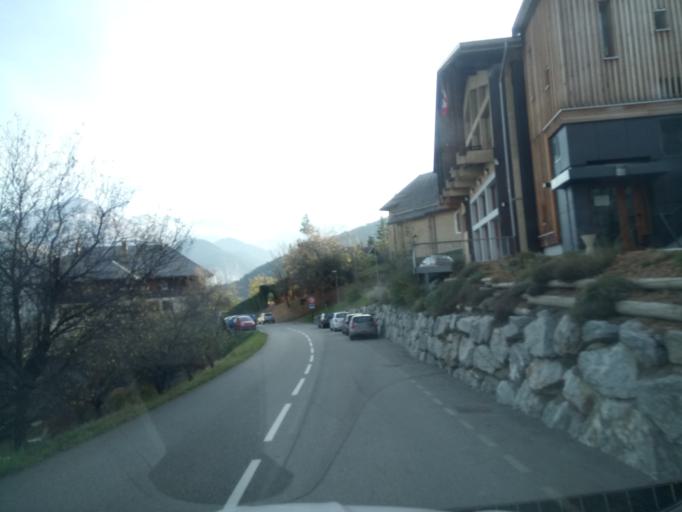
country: FR
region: Rhone-Alpes
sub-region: Departement de la Savoie
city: Saint-Jean-de-Maurienne
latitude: 45.2798
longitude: 6.3170
